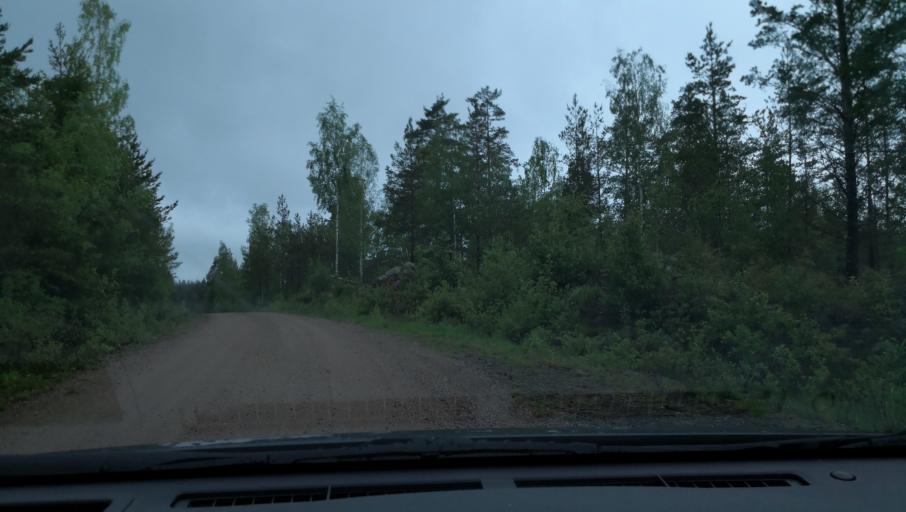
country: SE
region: Uppsala
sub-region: Enkopings Kommun
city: Orsundsbro
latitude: 59.9328
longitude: 17.3275
